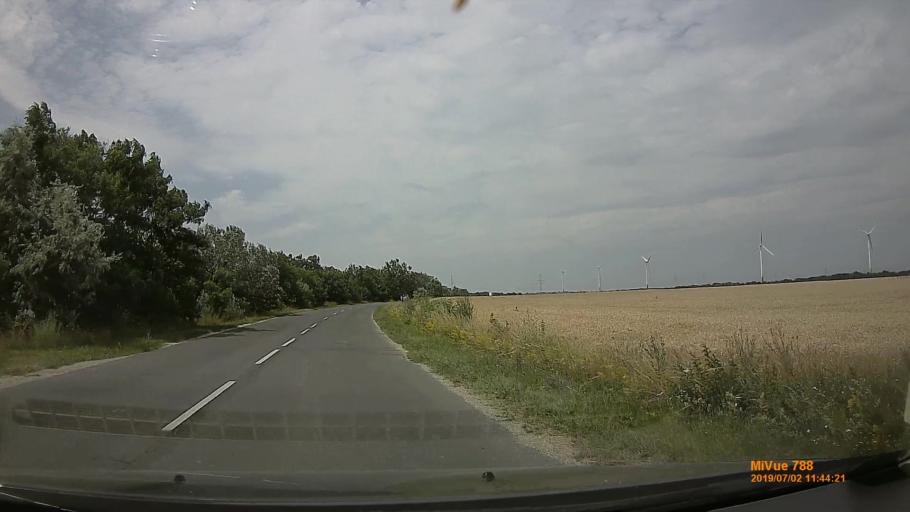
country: HU
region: Gyor-Moson-Sopron
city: Mosonmagyarovar
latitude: 47.8717
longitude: 17.2099
